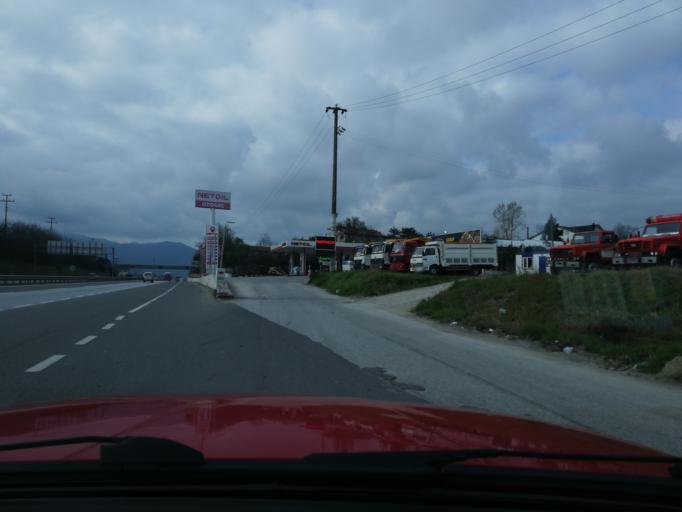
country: TR
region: Sakarya
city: Dogancay
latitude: 40.6890
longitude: 30.3674
